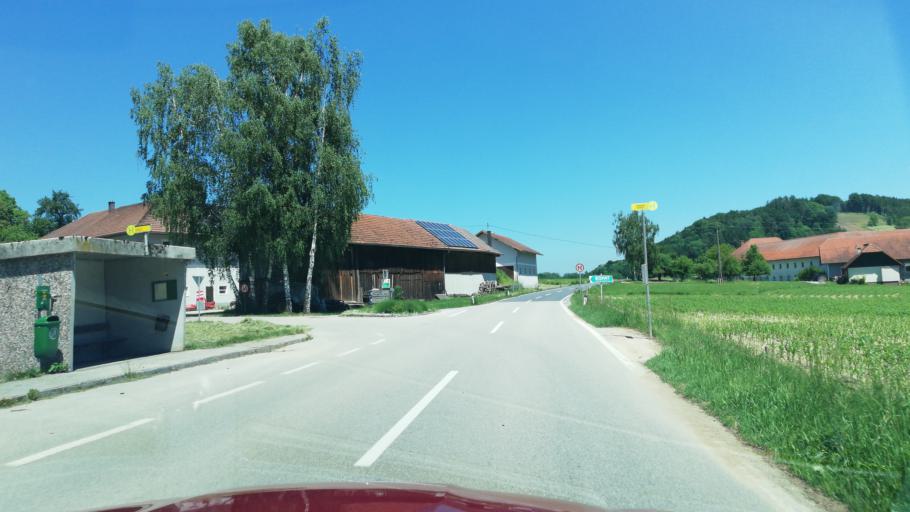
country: AT
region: Upper Austria
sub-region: Wels-Land
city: Bachmanning
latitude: 48.1382
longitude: 13.8015
